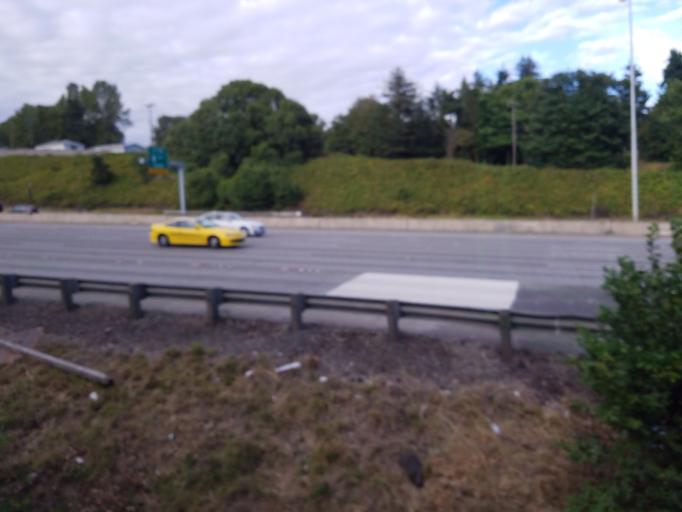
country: US
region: Washington
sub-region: King County
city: Tukwila
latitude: 47.4712
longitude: -122.2691
